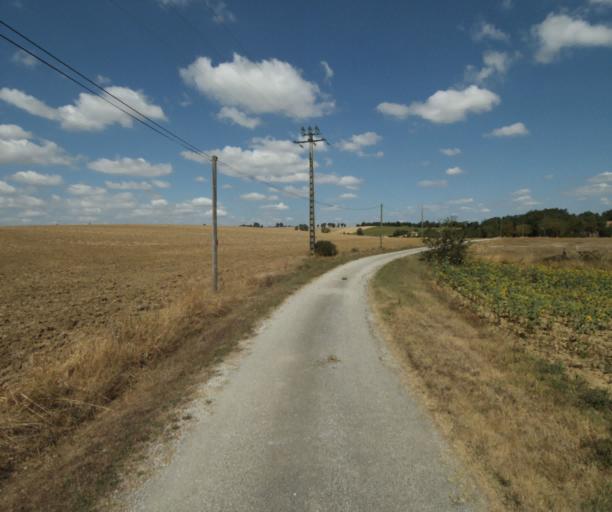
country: FR
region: Midi-Pyrenees
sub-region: Departement de la Haute-Garonne
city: Auriac-sur-Vendinelle
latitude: 43.4851
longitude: 1.8385
